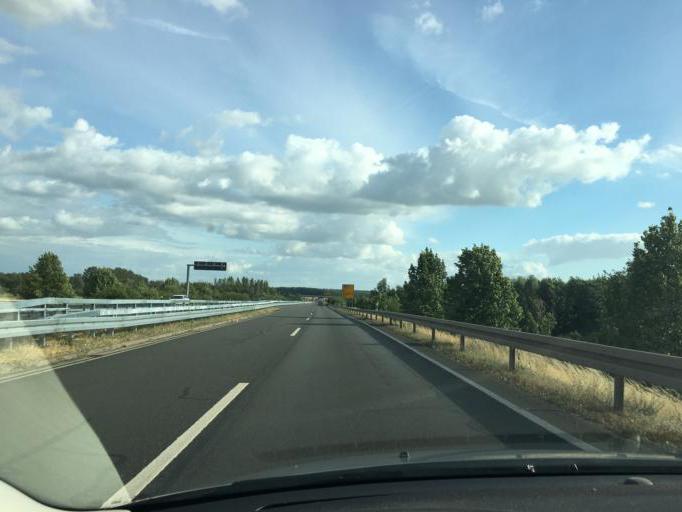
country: DE
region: Saxony-Anhalt
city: Wolmirstedt
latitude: 52.2502
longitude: 11.6029
